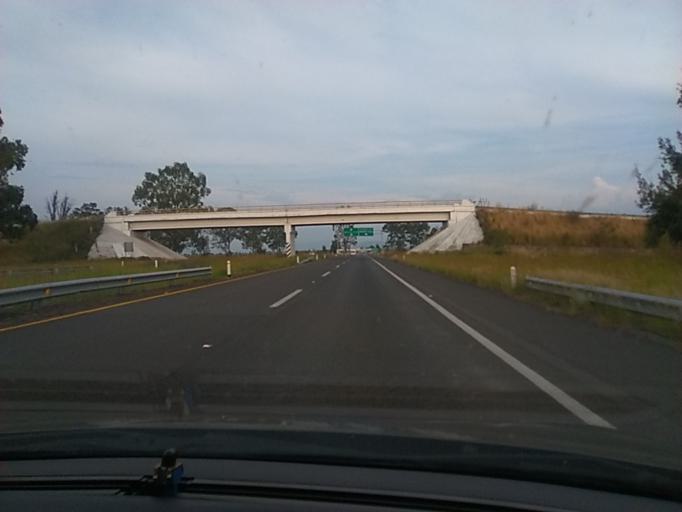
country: MX
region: Michoacan
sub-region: Alvaro Obregon
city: Lazaro Cardenas (La Purisima)
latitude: 19.8914
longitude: -101.0212
